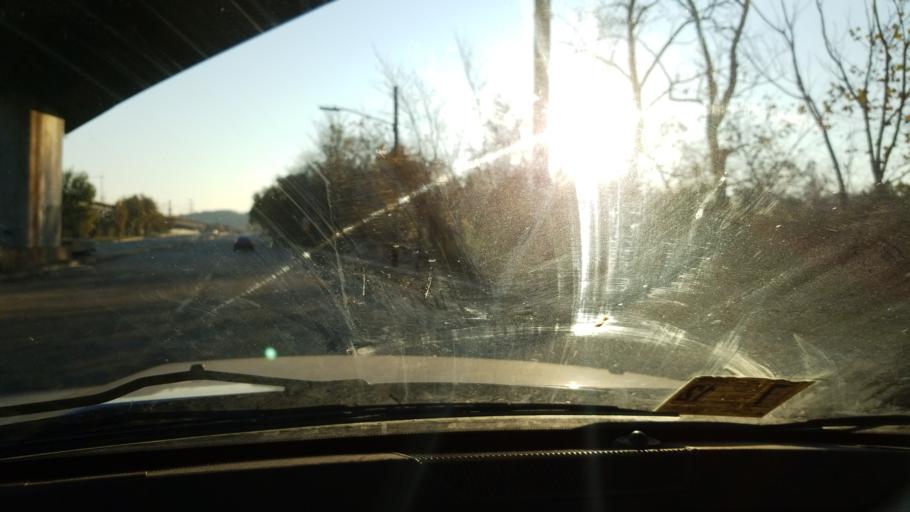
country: US
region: Maryland
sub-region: Prince George's County
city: Colmar Manor
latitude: 38.8970
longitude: -76.9662
